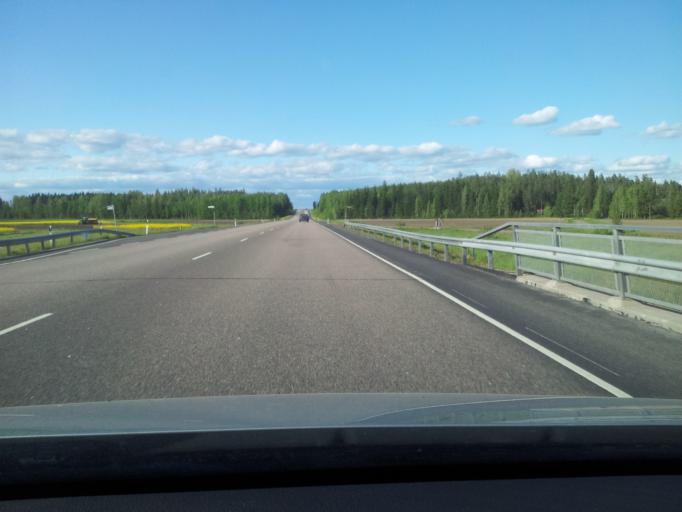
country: FI
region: Kymenlaakso
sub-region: Kouvola
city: Elimaeki
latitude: 60.8029
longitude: 26.5131
